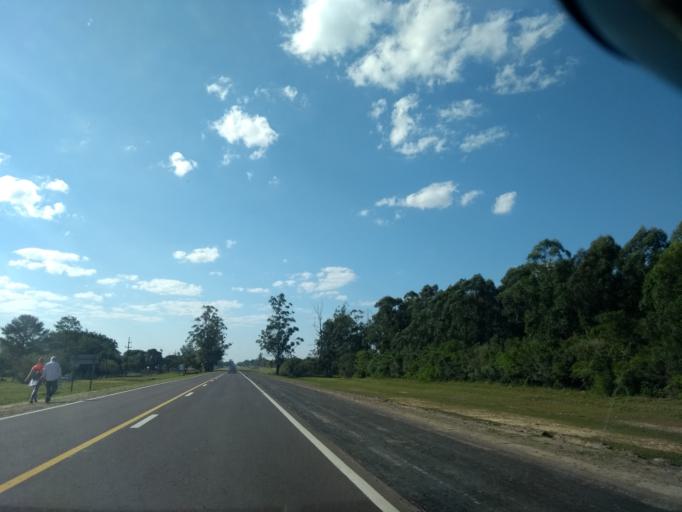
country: AR
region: Corrientes
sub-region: Departamento de San Cosme
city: San Cosme
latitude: -27.3672
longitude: -58.3642
